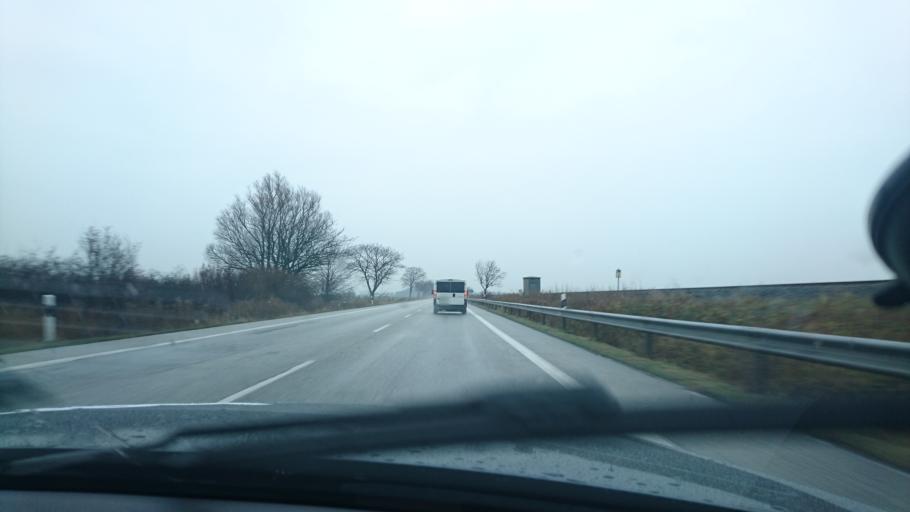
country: DE
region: Schleswig-Holstein
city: Fehmarn
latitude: 54.4364
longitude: 11.1522
